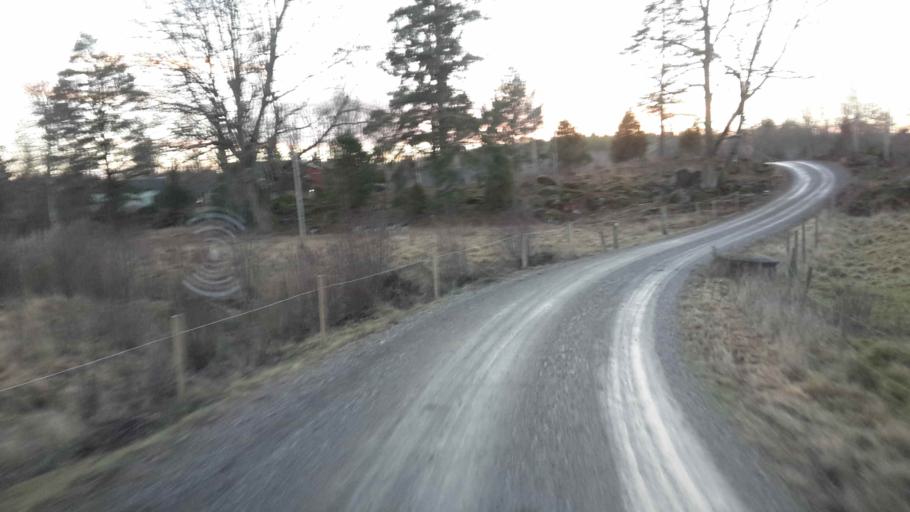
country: SE
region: OEstergoetland
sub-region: Atvidabergs Kommun
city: Atvidaberg
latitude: 58.2710
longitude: 16.0764
